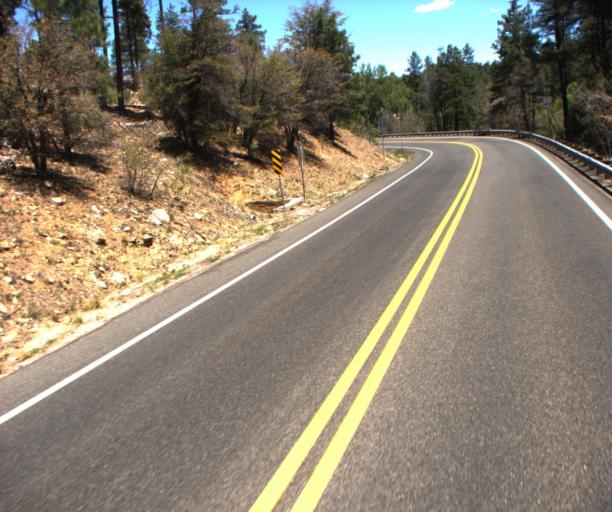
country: US
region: Arizona
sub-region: Yavapai County
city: Prescott
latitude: 34.5034
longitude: -112.4796
